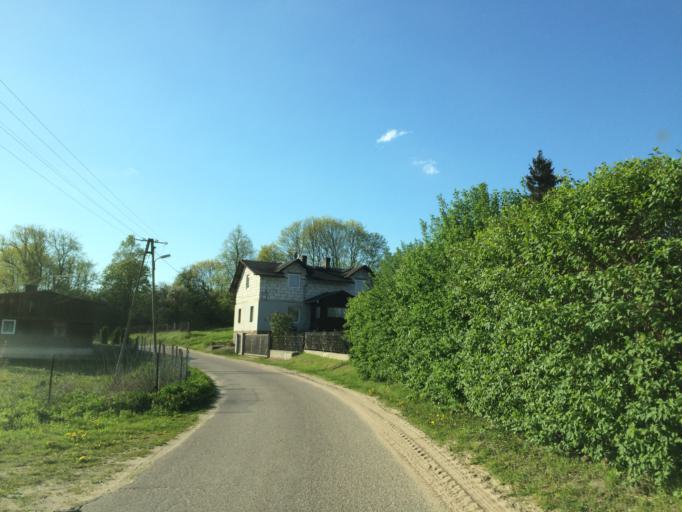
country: PL
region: Warmian-Masurian Voivodeship
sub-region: Powiat dzialdowski
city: Lidzbark
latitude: 53.2383
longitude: 19.7613
